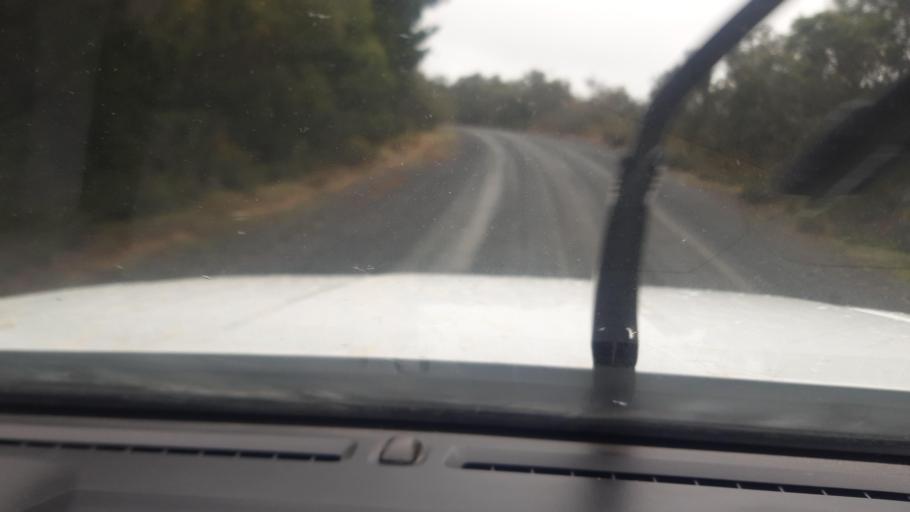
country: NZ
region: Northland
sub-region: Far North District
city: Kaitaia
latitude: -34.9867
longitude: 173.2129
